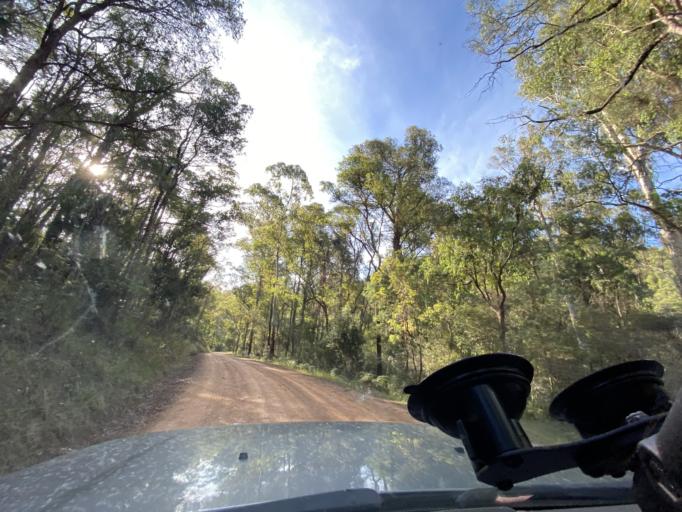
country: AU
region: Victoria
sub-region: Mansfield
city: Mansfield
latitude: -37.5201
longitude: 146.0759
